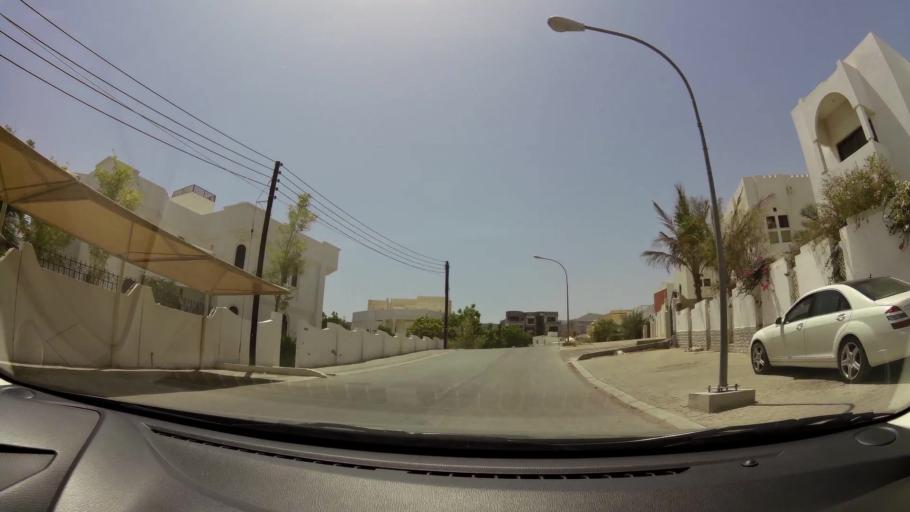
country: OM
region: Muhafazat Masqat
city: Bawshar
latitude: 23.5896
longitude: 58.4489
